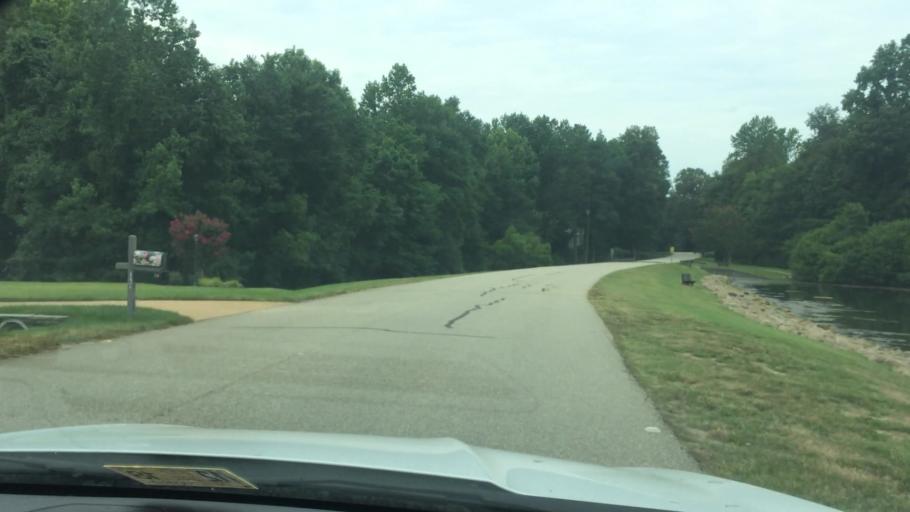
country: US
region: Virginia
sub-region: James City County
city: Williamsburg
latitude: 37.3027
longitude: -76.7704
